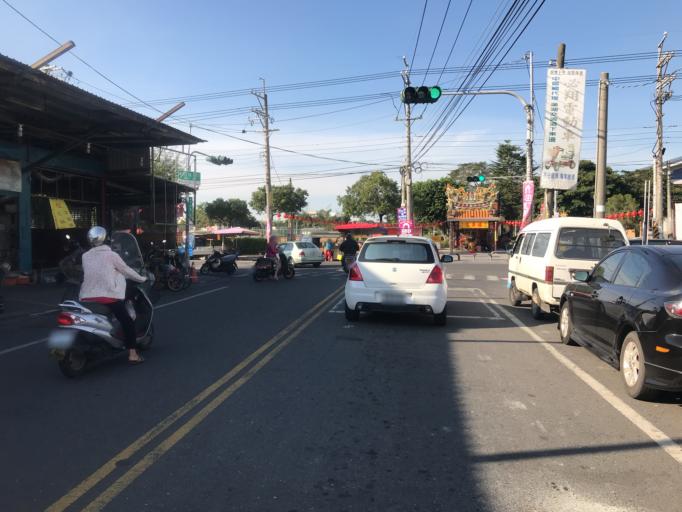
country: TW
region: Taiwan
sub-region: Nantou
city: Nantou
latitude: 23.8568
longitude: 120.5818
